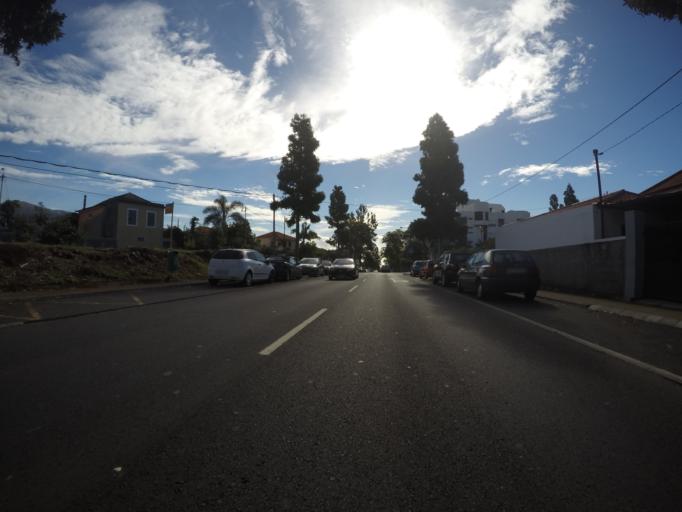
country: PT
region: Madeira
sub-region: Funchal
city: Nossa Senhora do Monte
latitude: 32.6580
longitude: -16.9270
